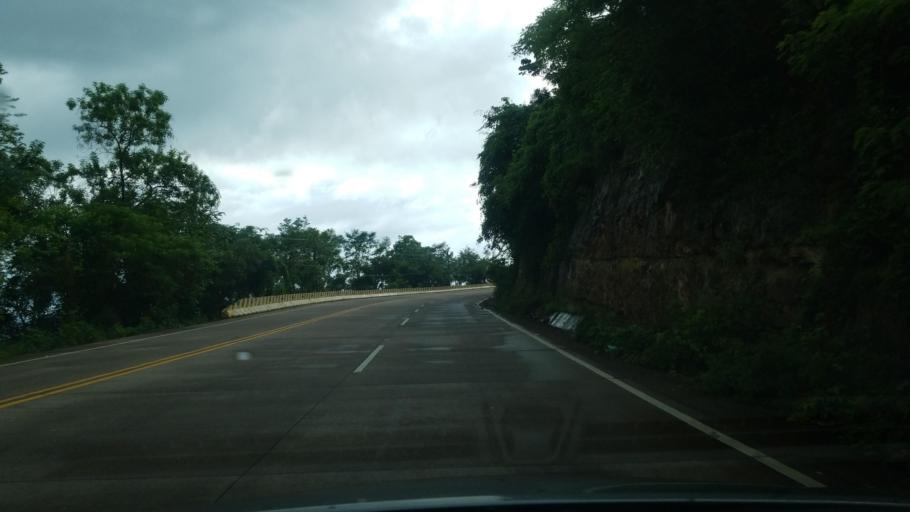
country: HN
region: Copan
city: Copan
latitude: 14.8363
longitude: -89.1837
